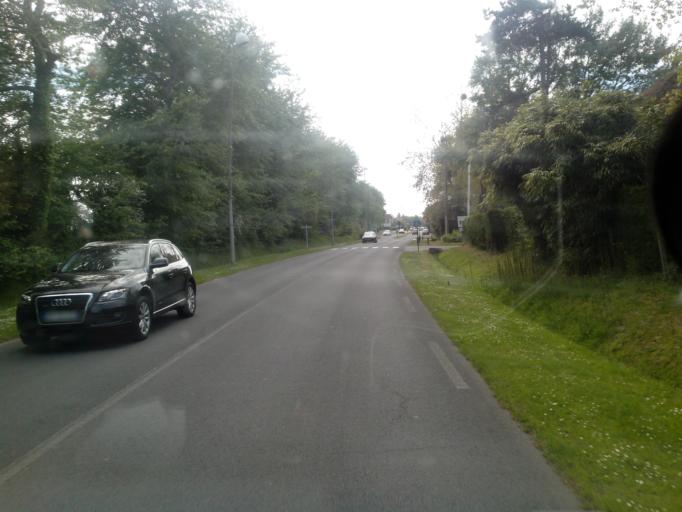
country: FR
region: Lower Normandy
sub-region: Departement du Calvados
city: Cabourg
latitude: 49.2844
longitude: -0.1507
